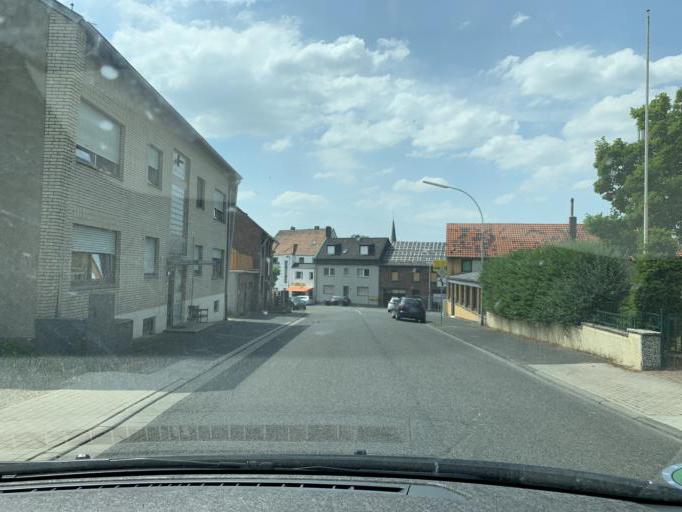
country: DE
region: North Rhine-Westphalia
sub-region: Regierungsbezirk Koln
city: Bedburg
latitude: 51.0386
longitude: 6.5991
